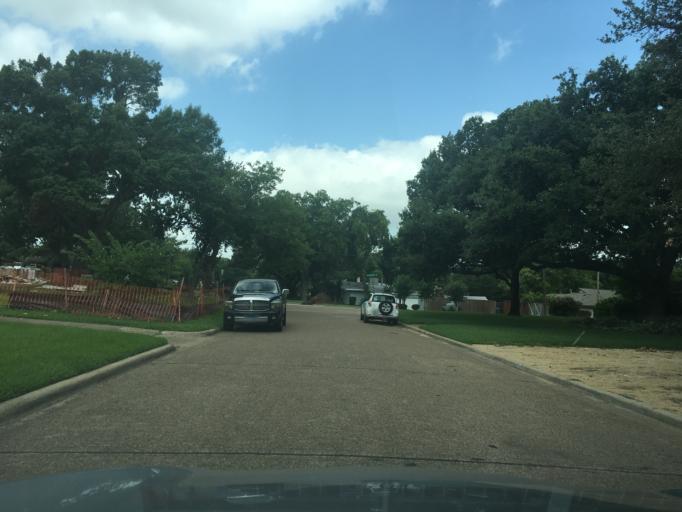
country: US
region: Texas
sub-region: Dallas County
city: Addison
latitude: 32.9132
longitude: -96.8333
